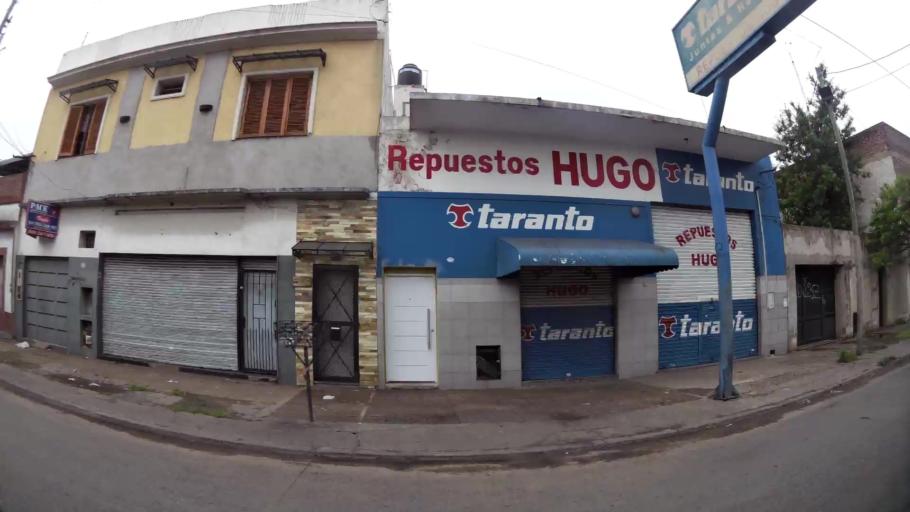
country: AR
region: Buenos Aires
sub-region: Partido de Lanus
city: Lanus
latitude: -34.7085
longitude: -58.3688
